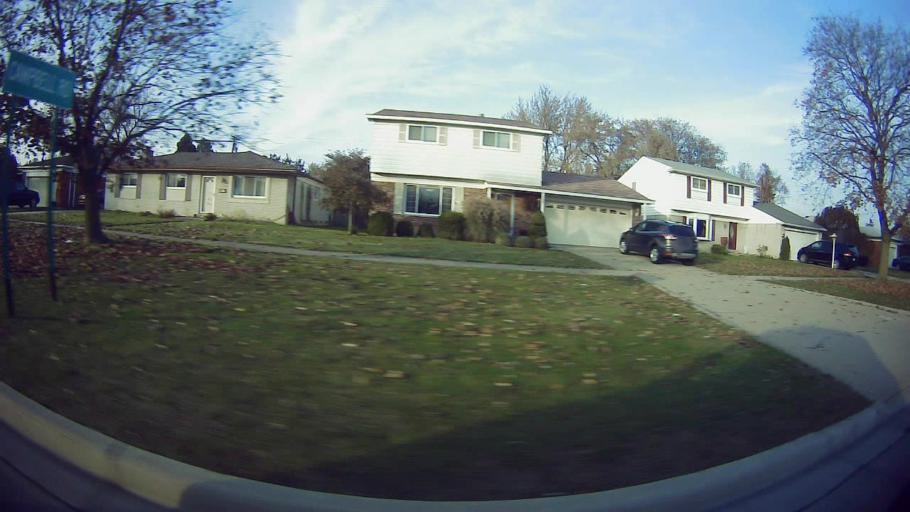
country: US
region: Michigan
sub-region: Oakland County
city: Clawson
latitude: 42.5196
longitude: -83.1248
